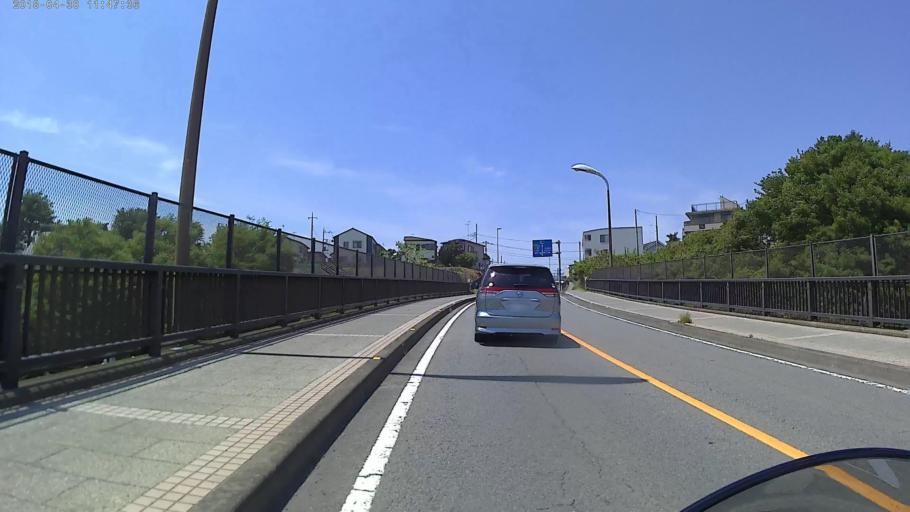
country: JP
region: Kanagawa
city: Zama
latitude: 35.4863
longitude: 139.3682
